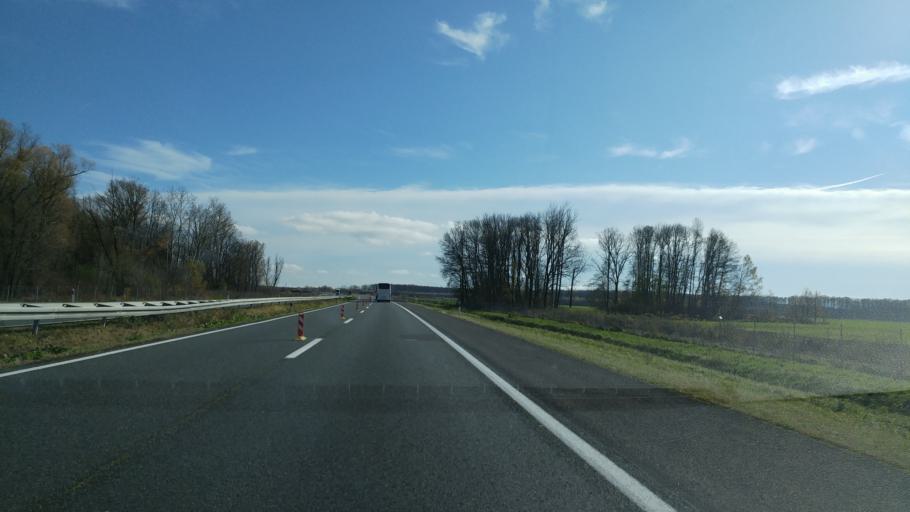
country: HR
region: Sisacko-Moslavacka
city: Lipovljani
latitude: 45.3786
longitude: 16.8753
